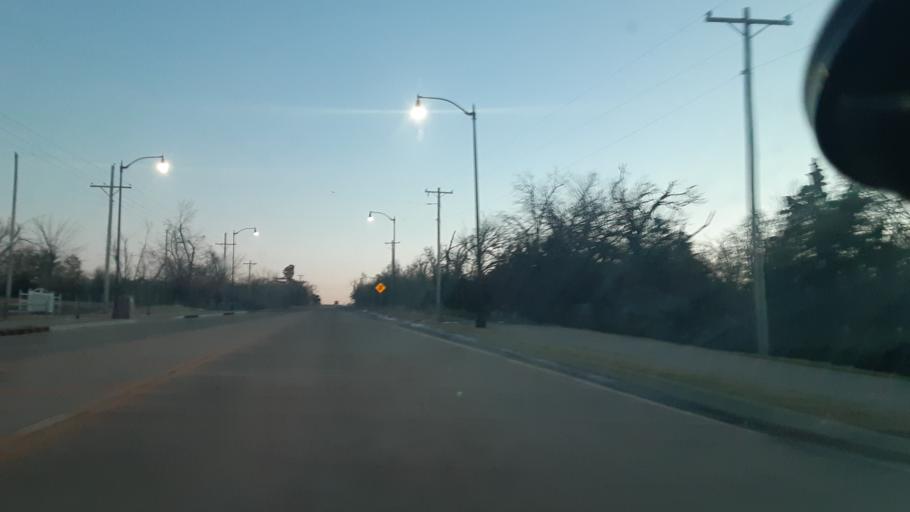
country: US
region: Oklahoma
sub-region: Oklahoma County
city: Edmond
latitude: 35.6791
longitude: -97.4251
